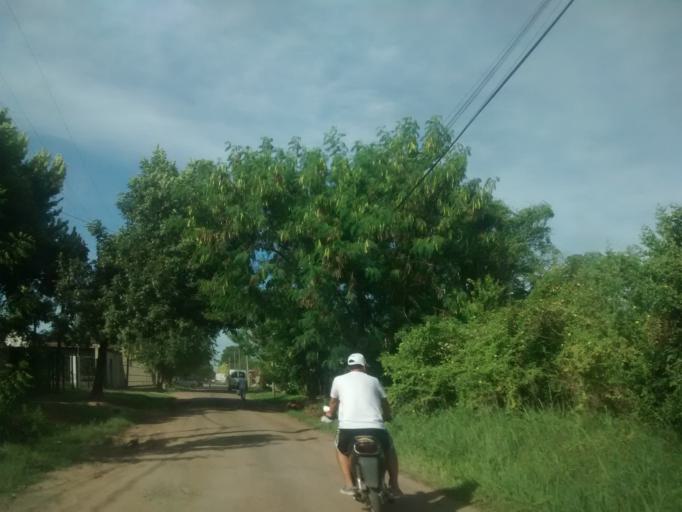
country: AR
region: Chaco
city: Puerto Tirol
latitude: -27.3737
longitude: -59.0932
